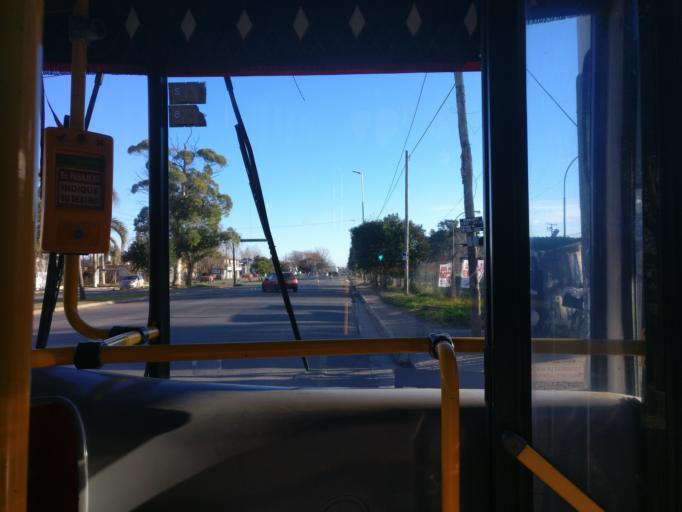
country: AR
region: Buenos Aires
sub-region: Partido de Ezeiza
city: Ezeiza
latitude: -34.9102
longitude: -58.5941
